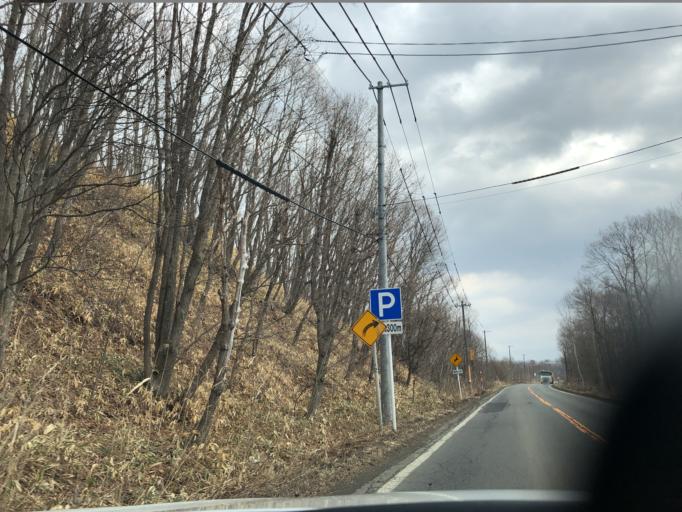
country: JP
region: Hokkaido
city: Chitose
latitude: 42.7667
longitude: 141.7132
